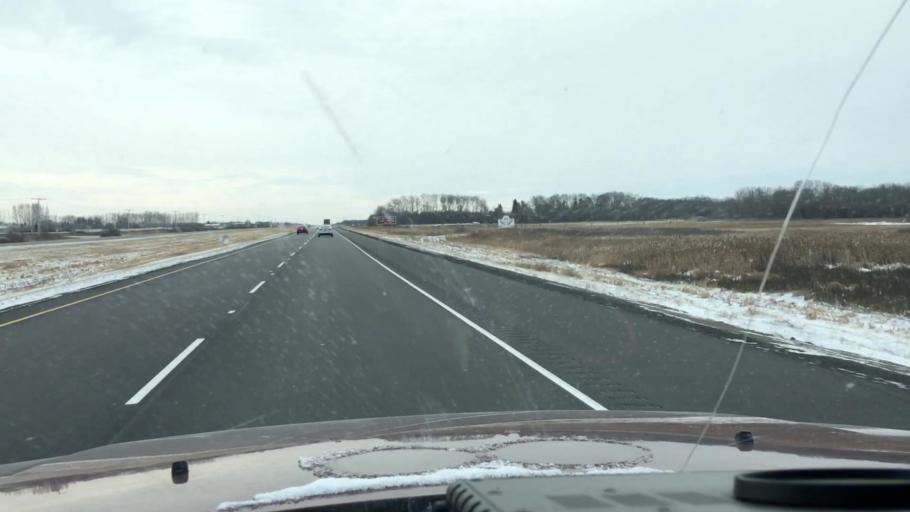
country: CA
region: Saskatchewan
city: Saskatoon
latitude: 51.9792
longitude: -106.5583
